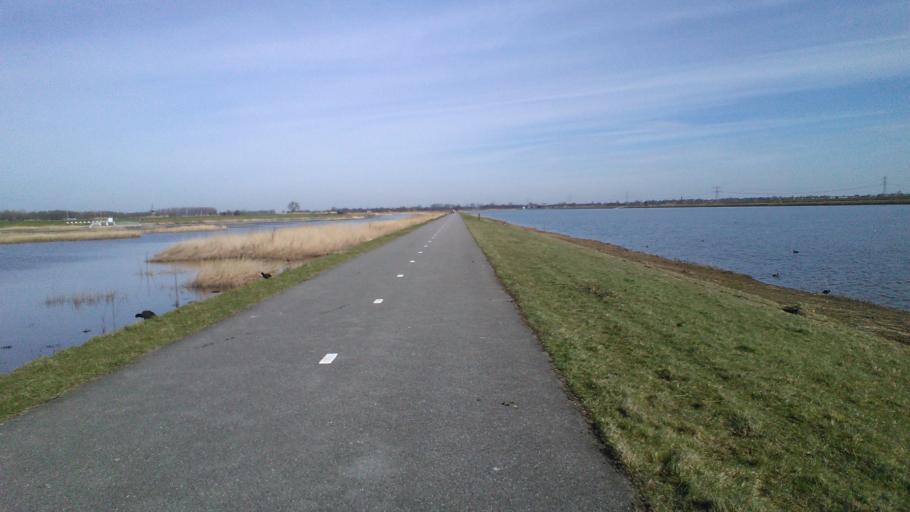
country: NL
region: South Holland
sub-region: Gemeente Lansingerland
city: Bleiswijk
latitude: 51.9920
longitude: 4.5569
